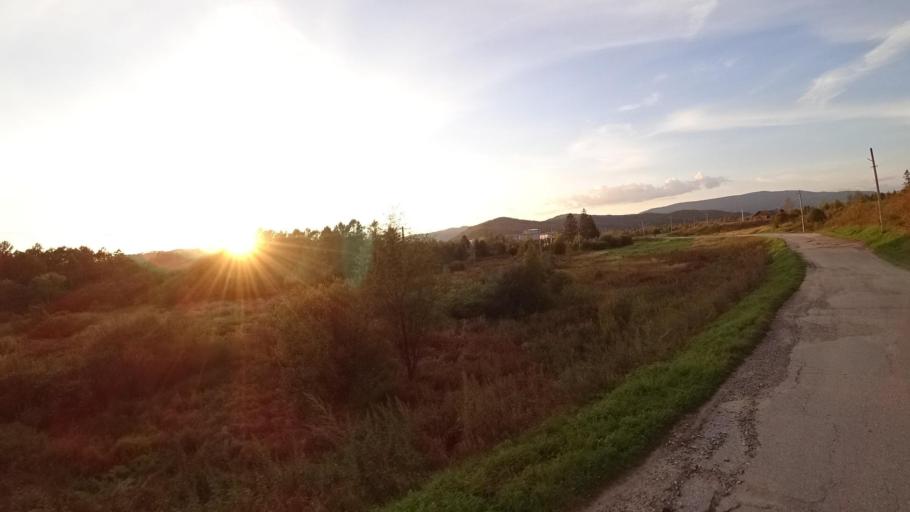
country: RU
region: Jewish Autonomous Oblast
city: Kul'dur
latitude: 49.1969
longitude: 131.6336
